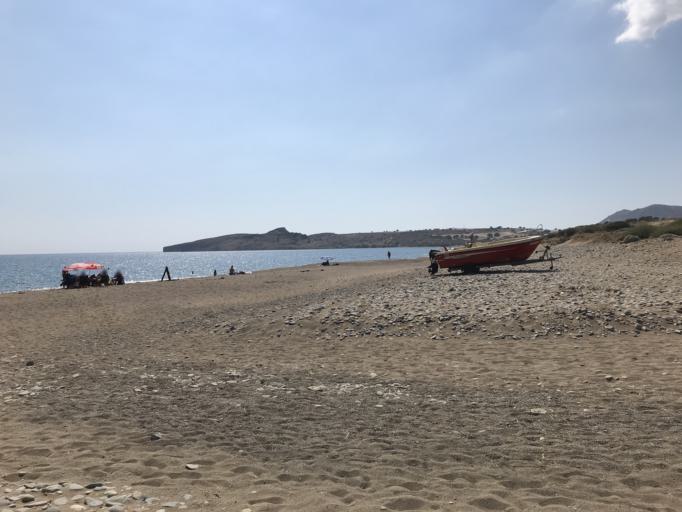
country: TR
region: Canakkale
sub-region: Goekceada
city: Gokceada
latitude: 40.1045
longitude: 25.8091
